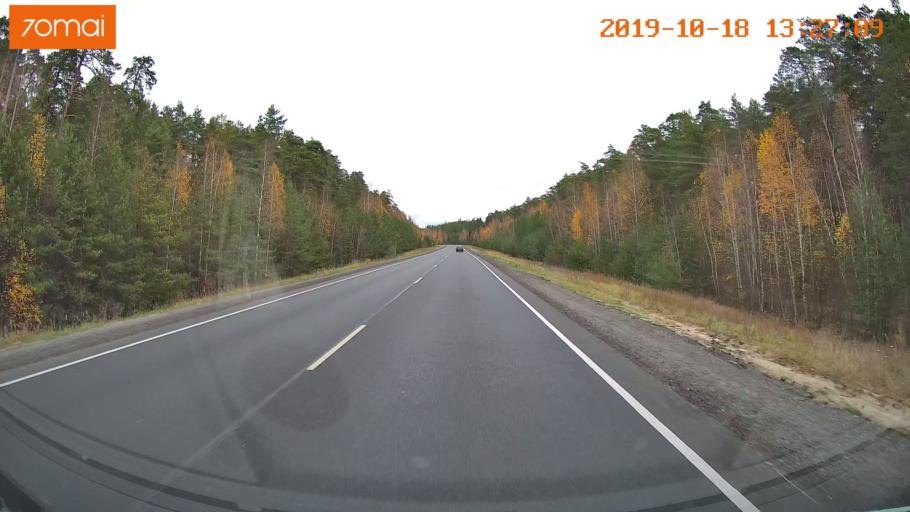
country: RU
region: Rjazan
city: Solotcha
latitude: 54.7608
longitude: 39.8495
